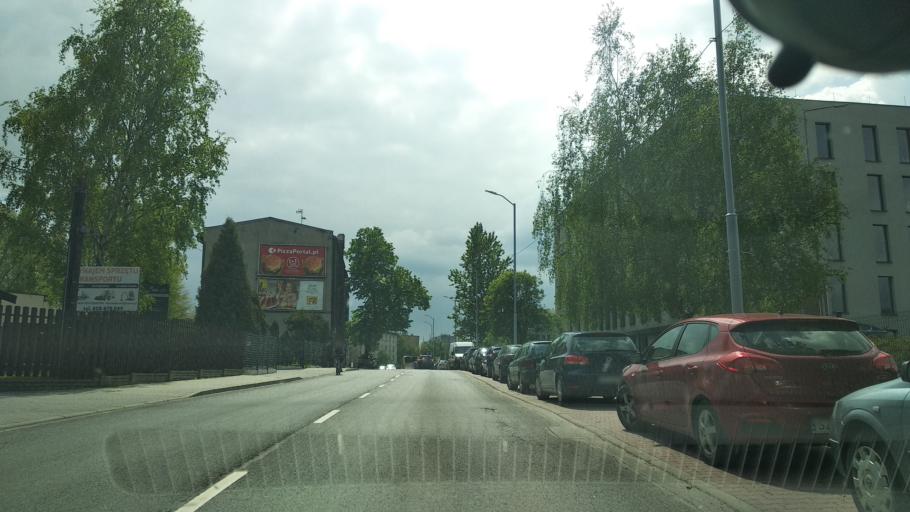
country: PL
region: Silesian Voivodeship
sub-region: Katowice
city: Katowice
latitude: 50.2371
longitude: 18.9789
